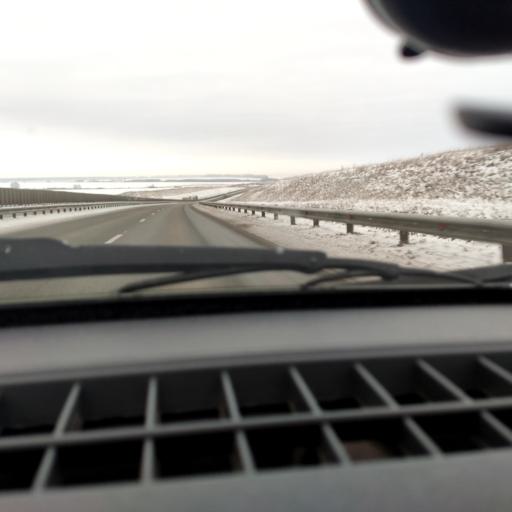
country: RU
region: Bashkortostan
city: Kushnarenkovo
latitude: 55.0653
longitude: 55.3080
